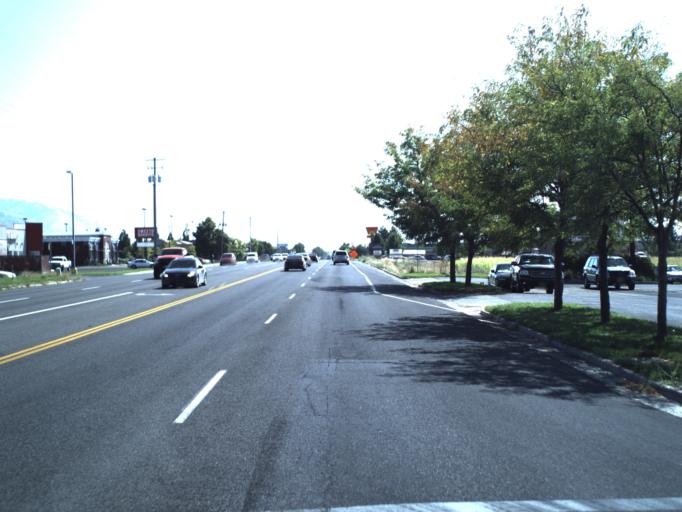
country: US
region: Utah
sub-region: Cache County
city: Logan
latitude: 41.7649
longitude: -111.8343
